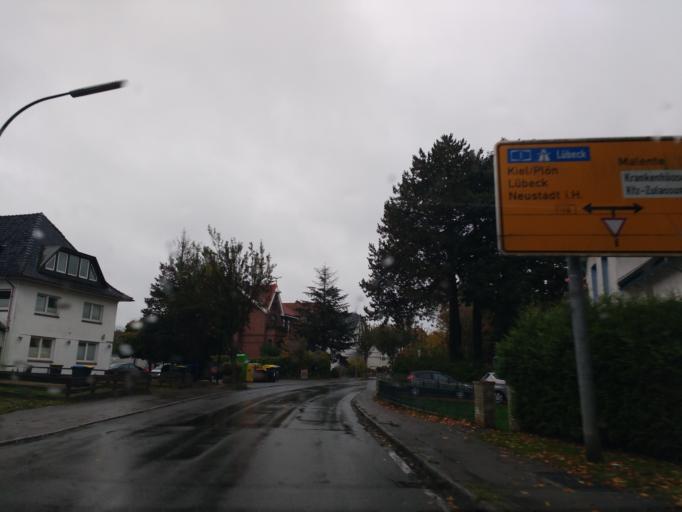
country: DE
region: Schleswig-Holstein
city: Eutin
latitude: 54.1304
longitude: 10.6237
